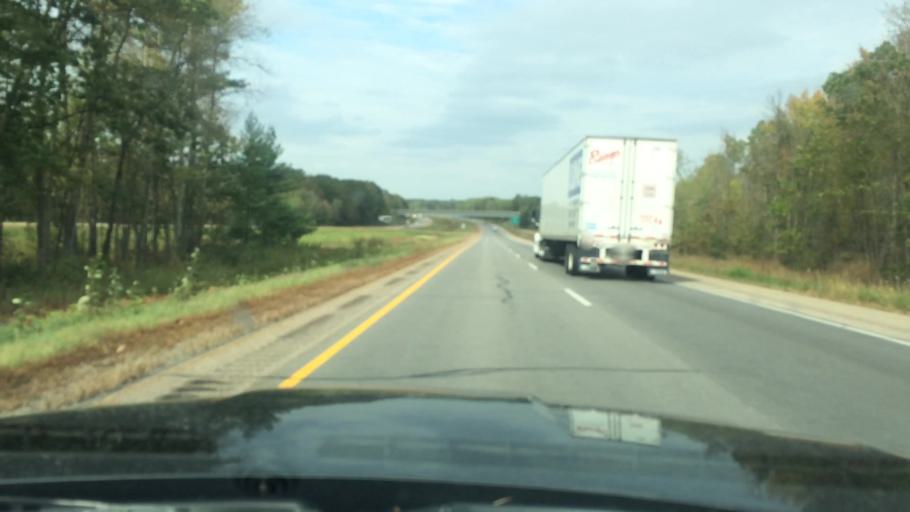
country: US
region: Wisconsin
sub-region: Marathon County
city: Mosinee
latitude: 44.7094
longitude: -89.6567
